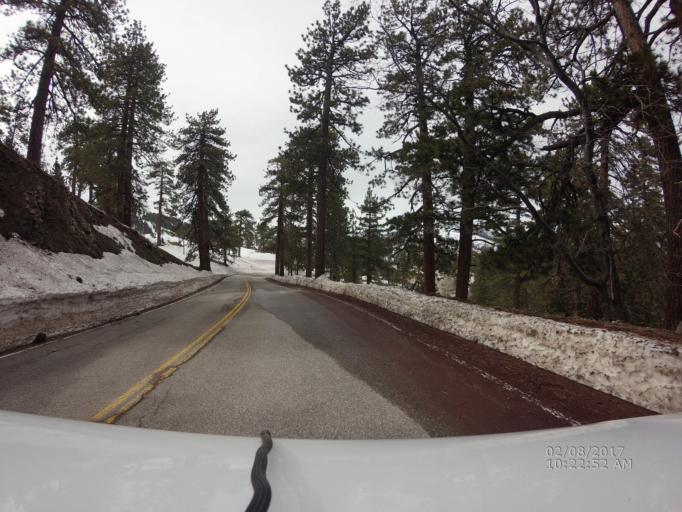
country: US
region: California
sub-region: San Bernardino County
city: Wrightwood
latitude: 34.3829
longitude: -117.6885
